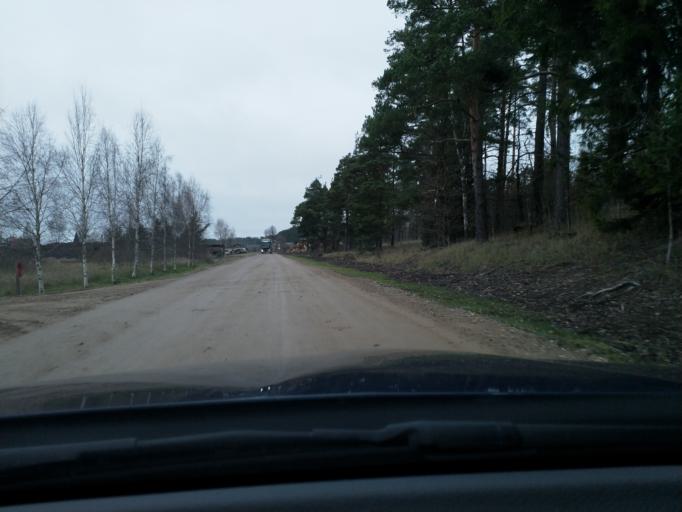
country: LV
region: Ventspils Rajons
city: Piltene
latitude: 57.1278
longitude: 21.8019
